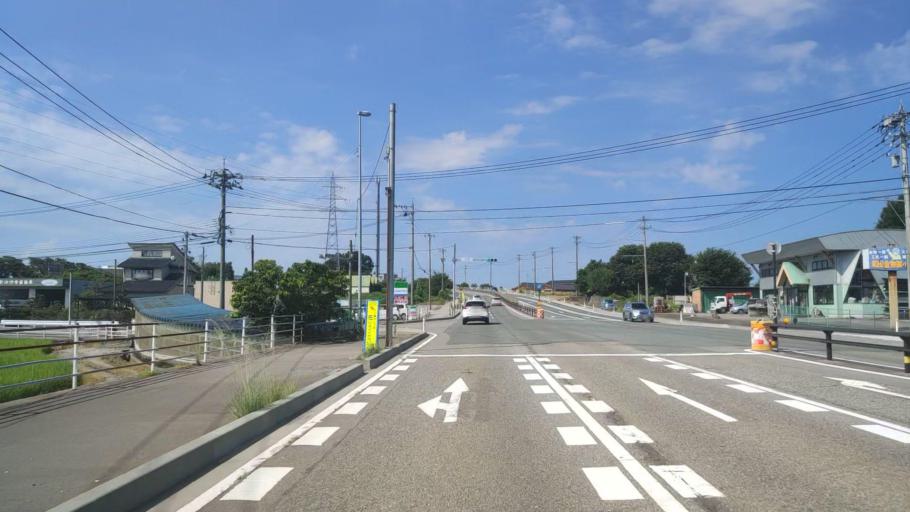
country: JP
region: Ishikawa
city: Komatsu
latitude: 36.4132
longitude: 136.5110
